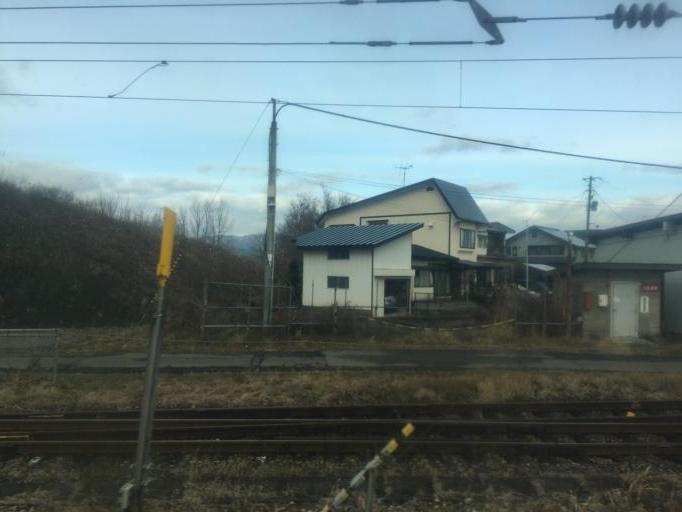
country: JP
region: Akita
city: Odate
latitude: 40.2893
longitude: 140.5613
